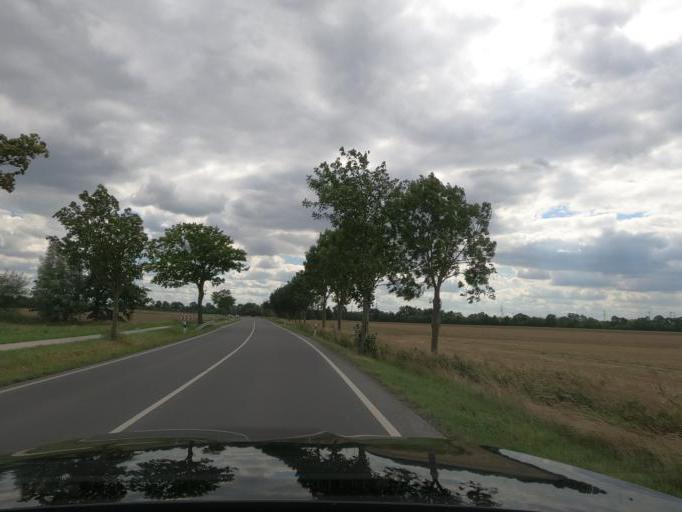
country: DE
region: Lower Saxony
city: Sehnde
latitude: 52.3141
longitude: 10.0284
